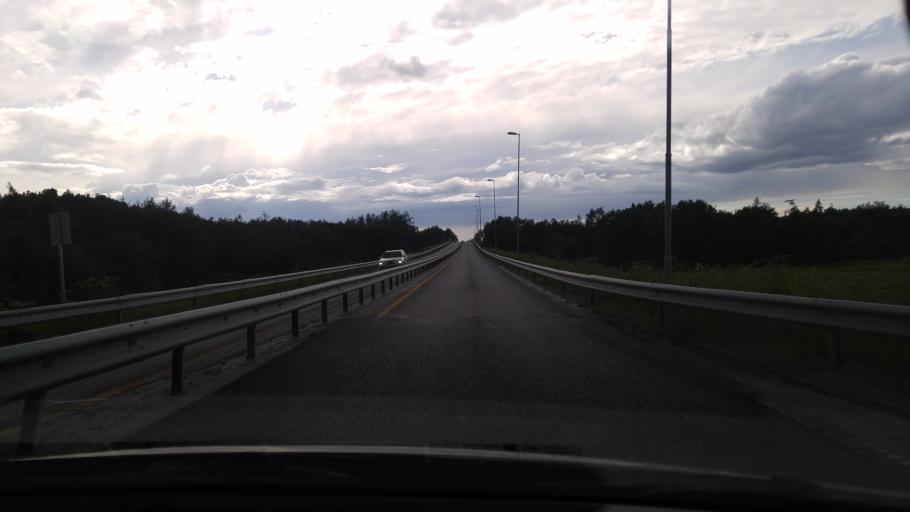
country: NO
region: Nord-Trondelag
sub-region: Levanger
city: Levanger
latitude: 63.7326
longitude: 11.3097
